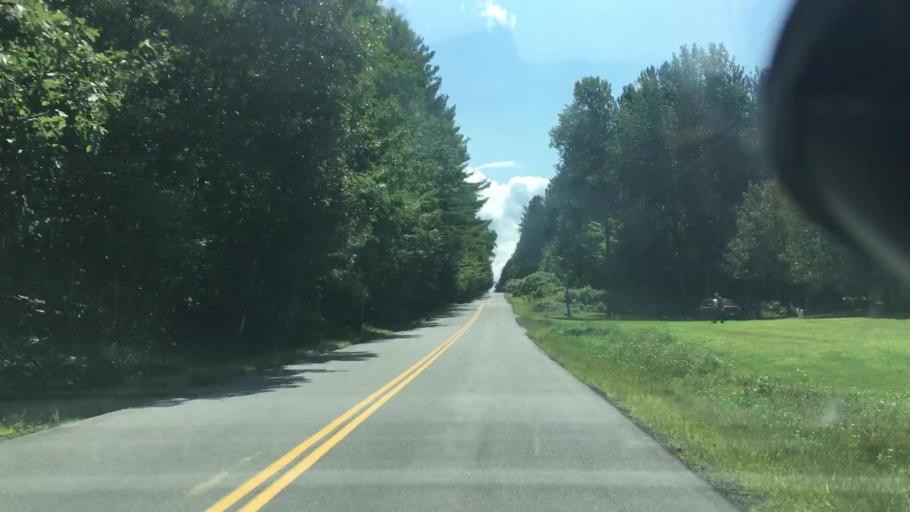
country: US
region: Maine
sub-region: Somerset County
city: Skowhegan
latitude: 44.7025
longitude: -69.6955
